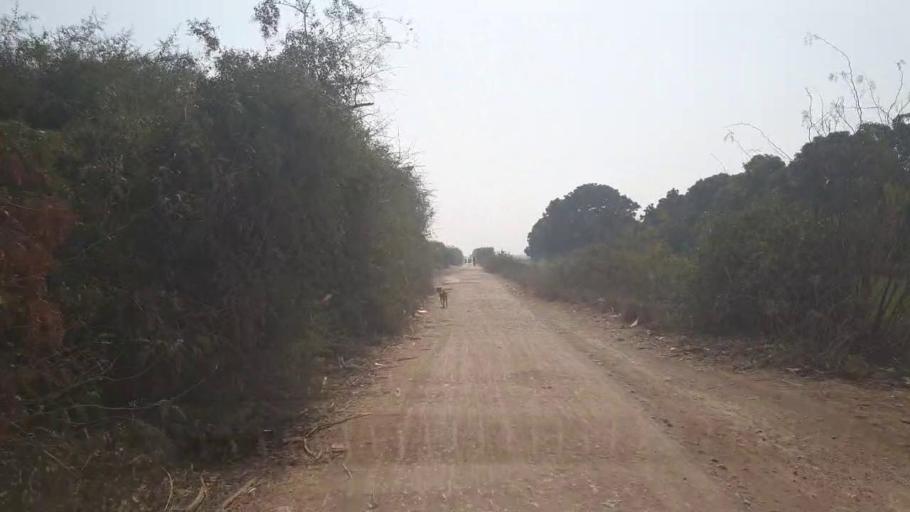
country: PK
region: Sindh
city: Tando Allahyar
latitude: 25.4819
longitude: 68.8022
